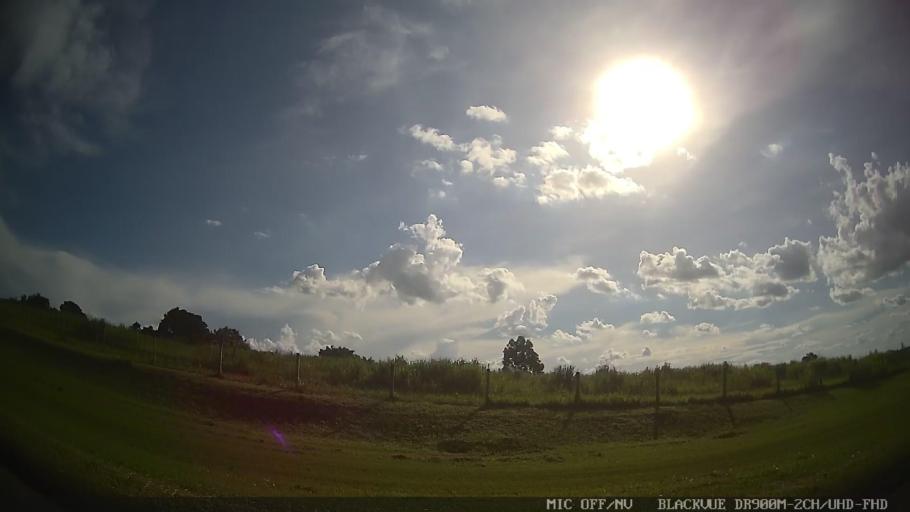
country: BR
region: Sao Paulo
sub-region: Laranjal Paulista
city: Laranjal Paulista
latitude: -23.0761
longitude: -47.8093
